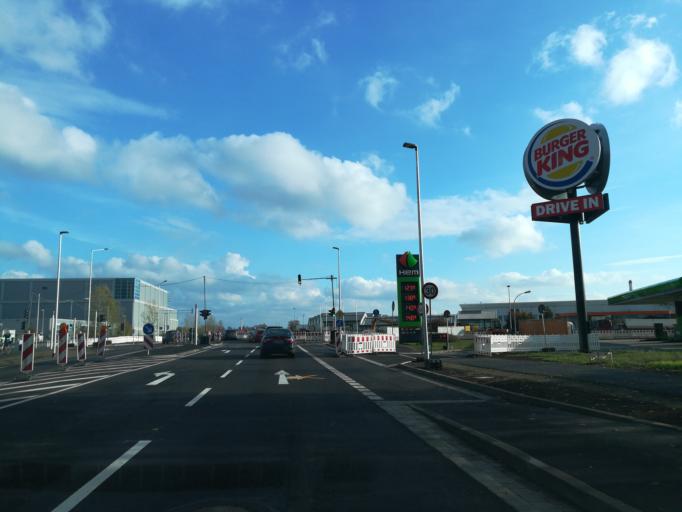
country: DE
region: Saxony-Anhalt
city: Haldensleben I
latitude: 52.2823
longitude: 11.4322
